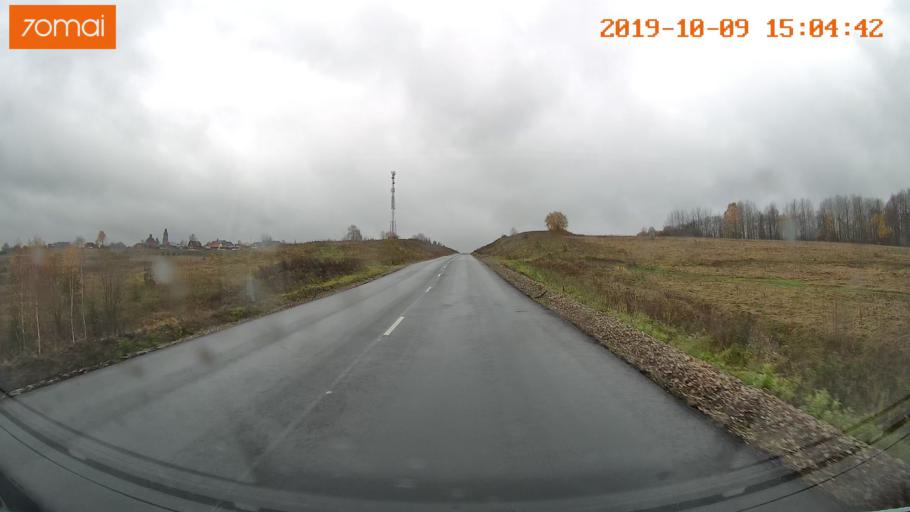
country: RU
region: Kostroma
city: Chistyye Bory
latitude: 58.2554
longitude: 41.6644
